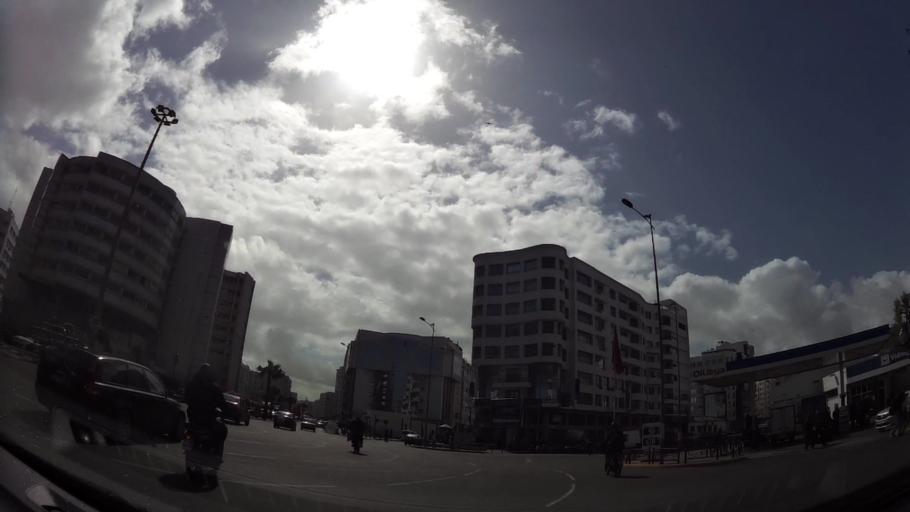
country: MA
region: Grand Casablanca
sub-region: Casablanca
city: Casablanca
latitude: 33.5902
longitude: -7.6039
